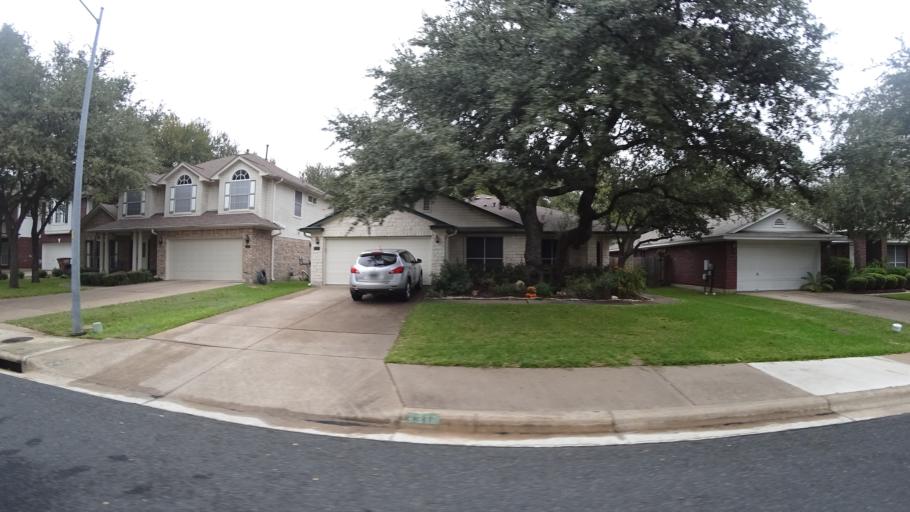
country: US
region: Texas
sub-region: Travis County
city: Shady Hollow
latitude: 30.1865
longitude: -97.8431
